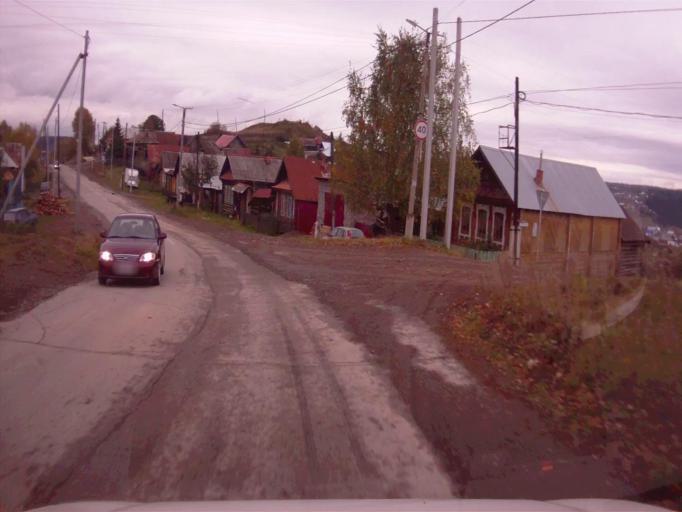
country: RU
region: Chelyabinsk
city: Nyazepetrovsk
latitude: 56.0609
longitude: 59.6133
